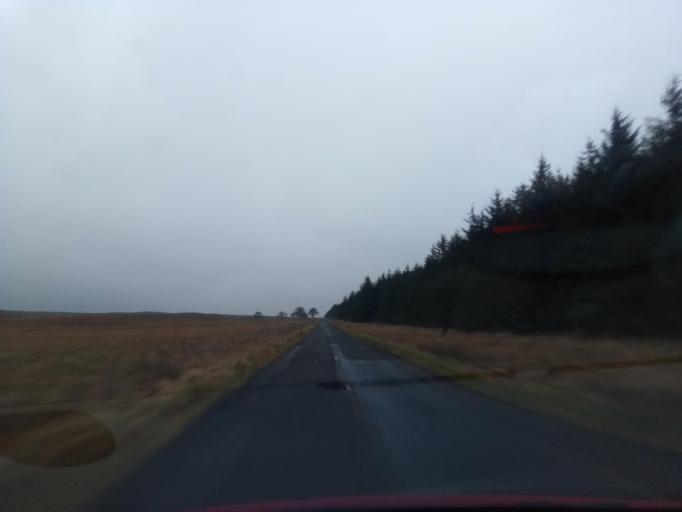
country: GB
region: England
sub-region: Northumberland
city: Rothley
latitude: 55.2067
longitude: -2.0277
